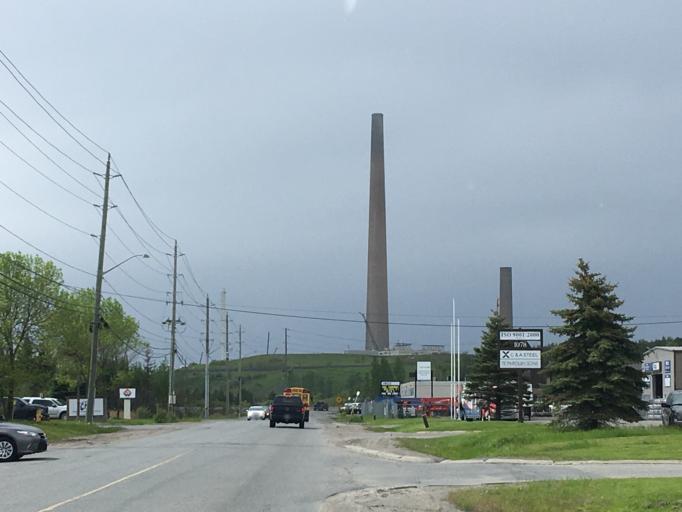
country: CA
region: Ontario
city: Greater Sudbury
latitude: 46.4682
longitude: -81.0343
